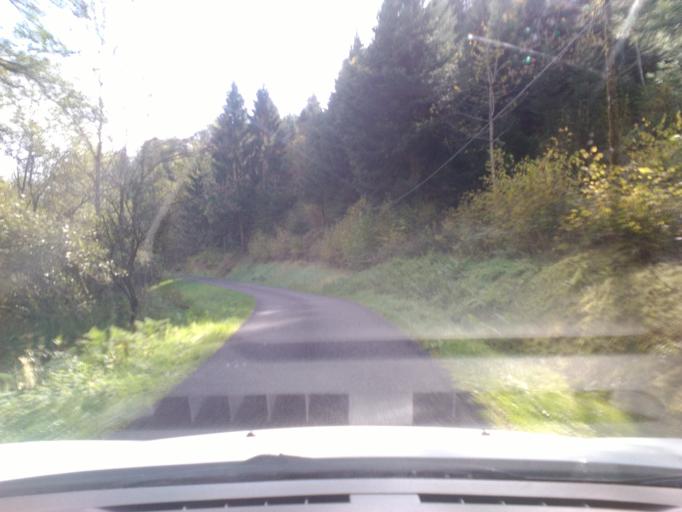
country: FR
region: Lorraine
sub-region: Departement des Vosges
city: Ban-de-Laveline
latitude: 48.2996
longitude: 7.0570
